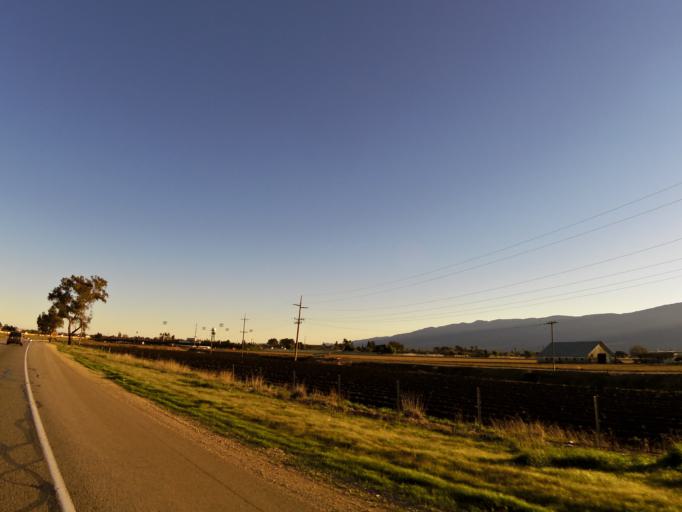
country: US
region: California
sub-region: Monterey County
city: Gonzales
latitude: 36.5205
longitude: -121.4458
